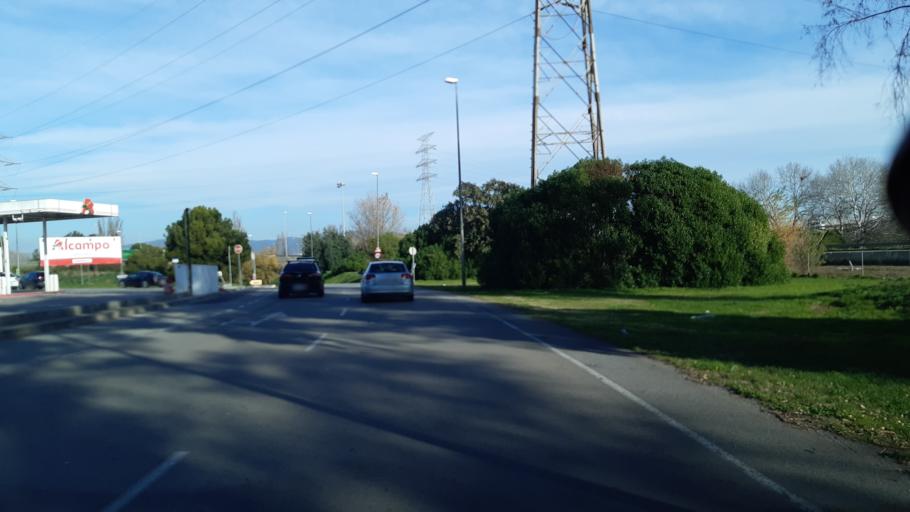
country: ES
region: Catalonia
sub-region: Provincia de Barcelona
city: Sant Boi de Llobregat
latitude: 41.3312
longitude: 2.0547
